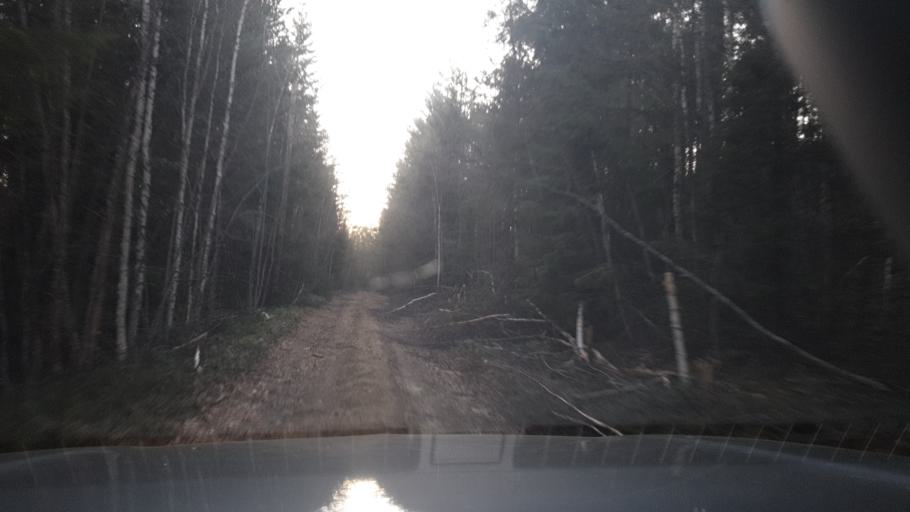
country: SE
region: Vaesternorrland
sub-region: Ange Kommun
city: Ange
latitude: 62.1878
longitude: 15.6114
